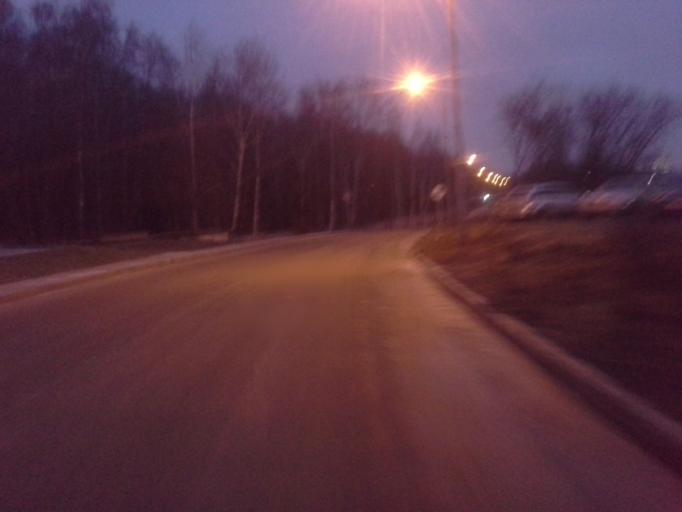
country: RU
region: Moskovskaya
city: Vostryakovo
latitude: 55.6594
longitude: 37.4533
